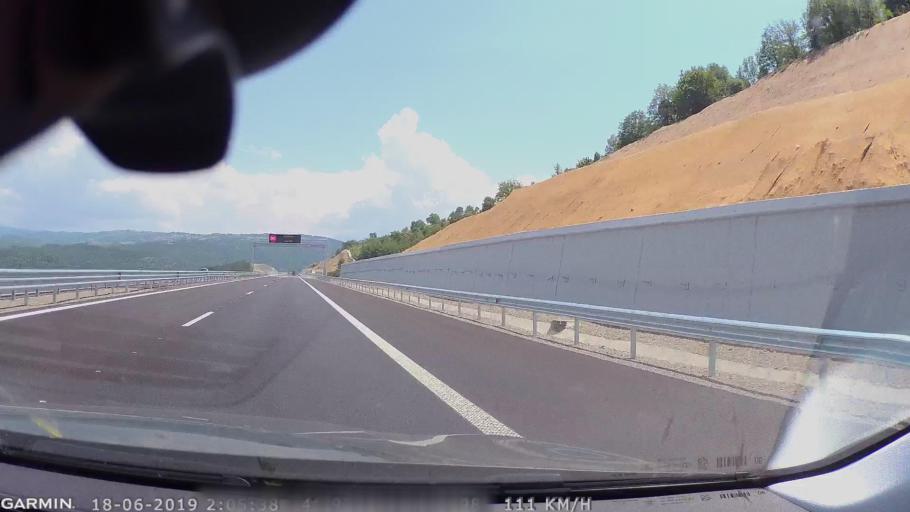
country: BG
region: Blagoevgrad
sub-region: Obshtina Blagoevgrad
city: Blagoevgrad
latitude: 41.9740
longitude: 23.0767
